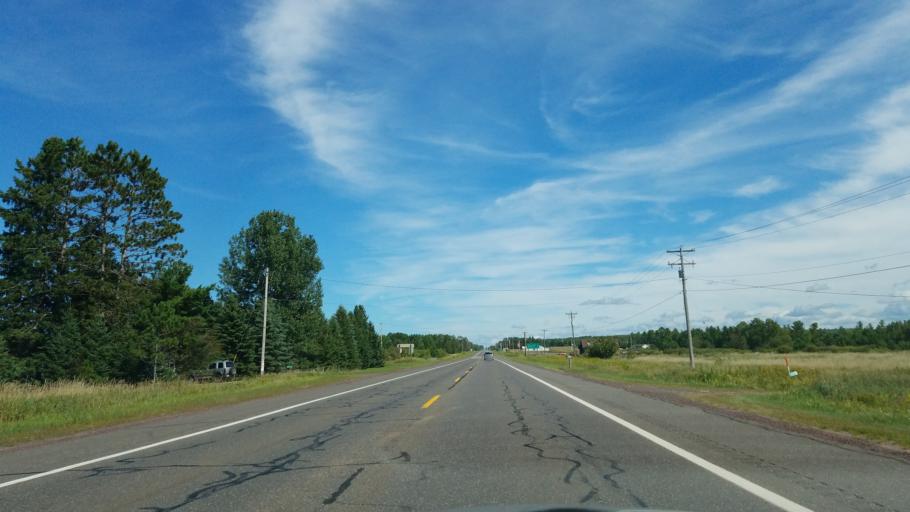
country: US
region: Michigan
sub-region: Ontonagon County
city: Ontonagon
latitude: 46.5348
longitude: -89.1742
